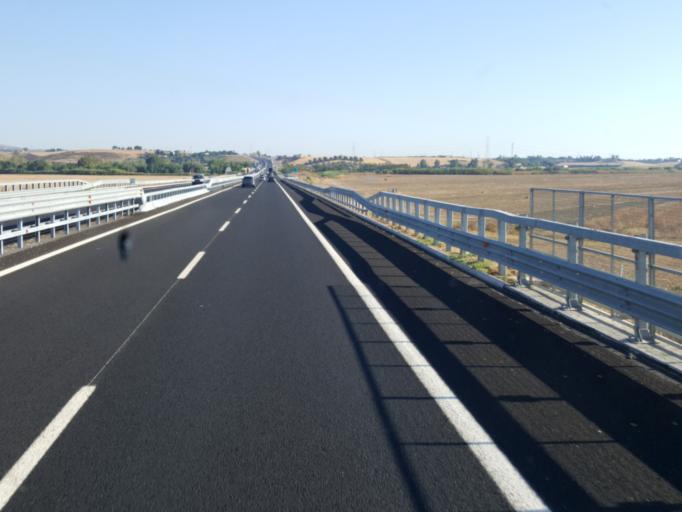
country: IT
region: Latium
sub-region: Provincia di Viterbo
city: Tarquinia
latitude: 42.2010
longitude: 11.7854
